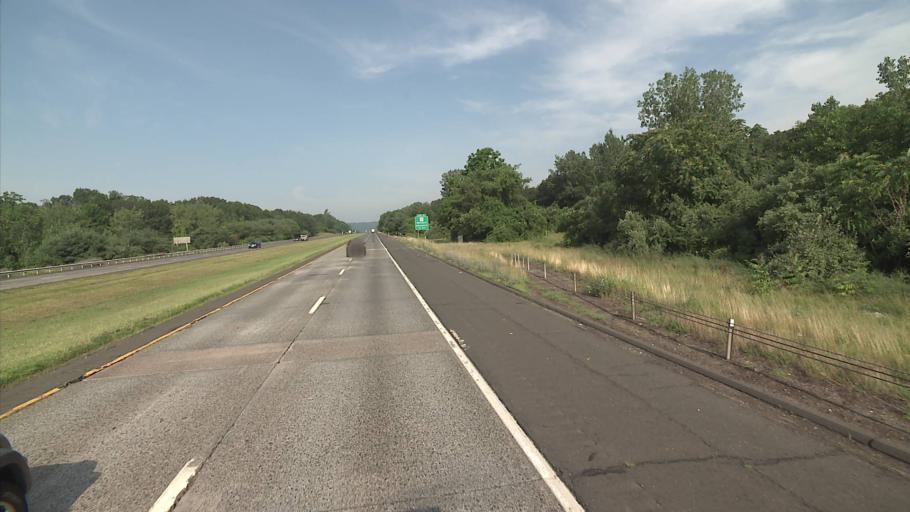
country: US
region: Connecticut
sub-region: New Haven County
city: Cheshire Village
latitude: 41.5557
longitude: -72.8741
